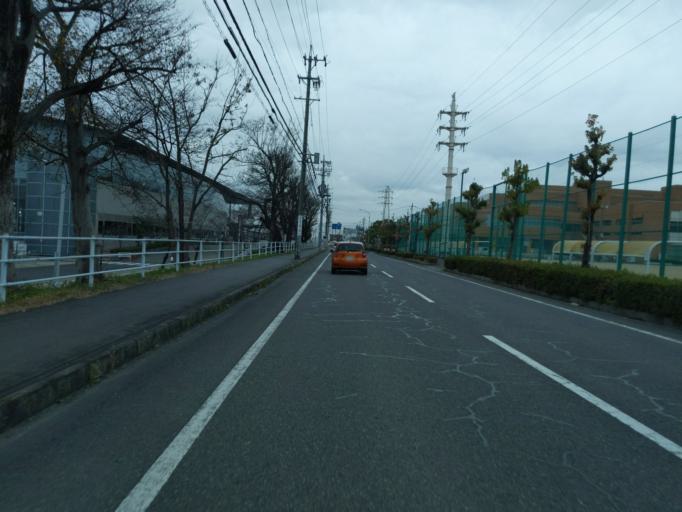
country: JP
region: Aichi
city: Kasugai
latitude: 35.2683
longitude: 136.9642
